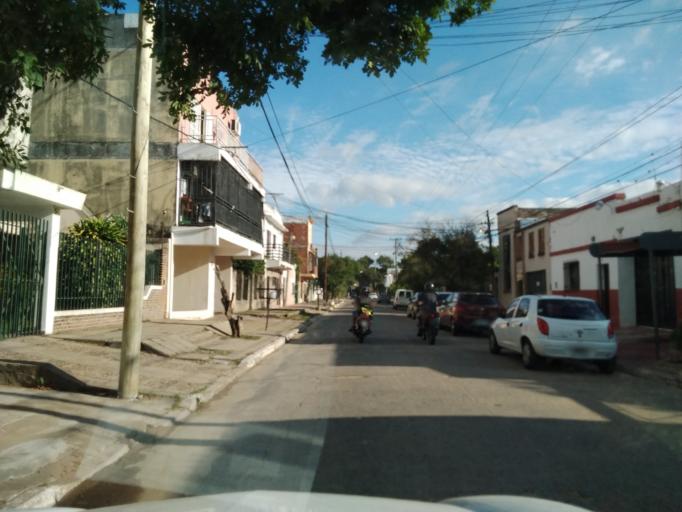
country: AR
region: Corrientes
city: Corrientes
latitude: -27.4647
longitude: -58.8193
